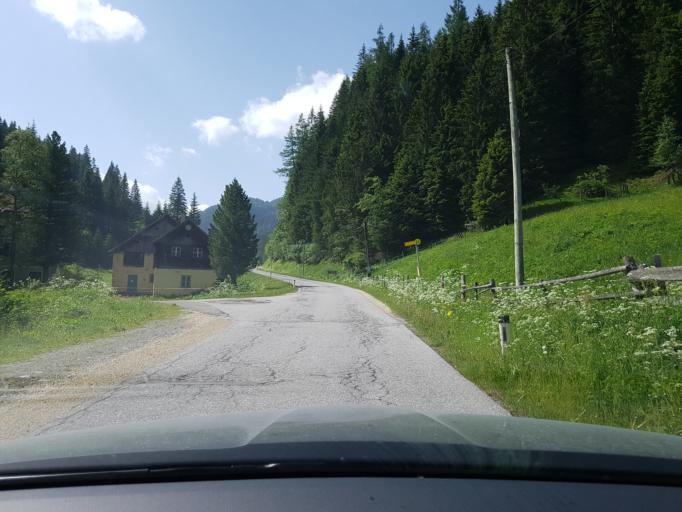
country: AT
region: Salzburg
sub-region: Politischer Bezirk Tamsweg
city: Thomatal
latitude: 47.0477
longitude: 13.7103
